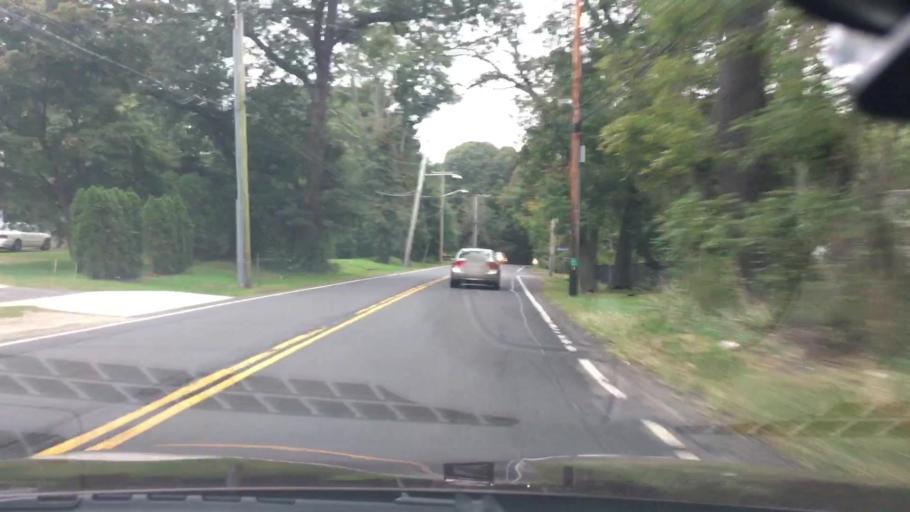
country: US
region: New York
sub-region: Suffolk County
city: Hauppauge
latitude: 40.8179
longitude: -73.2136
